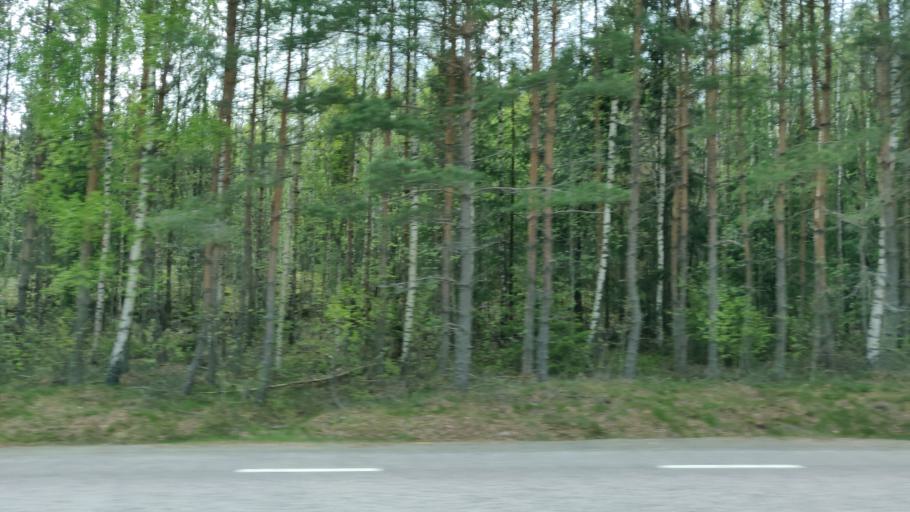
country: SE
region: Vaermland
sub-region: Forshaga Kommun
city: Deje
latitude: 59.6124
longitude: 13.4487
